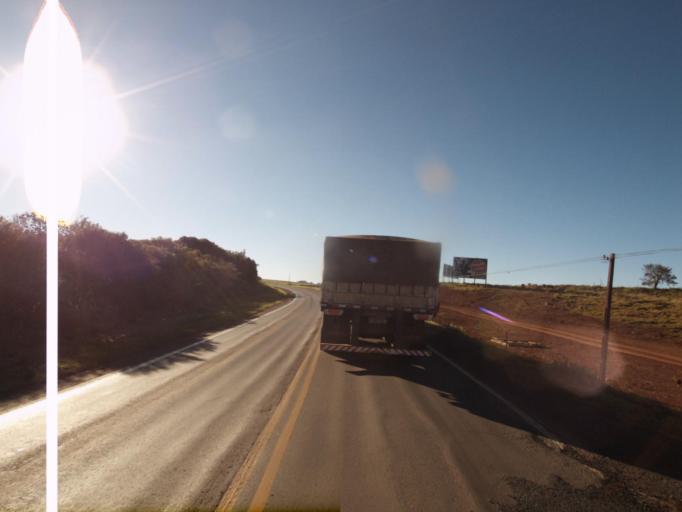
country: AR
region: Misiones
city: Bernardo de Irigoyen
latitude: -26.3081
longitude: -53.5470
